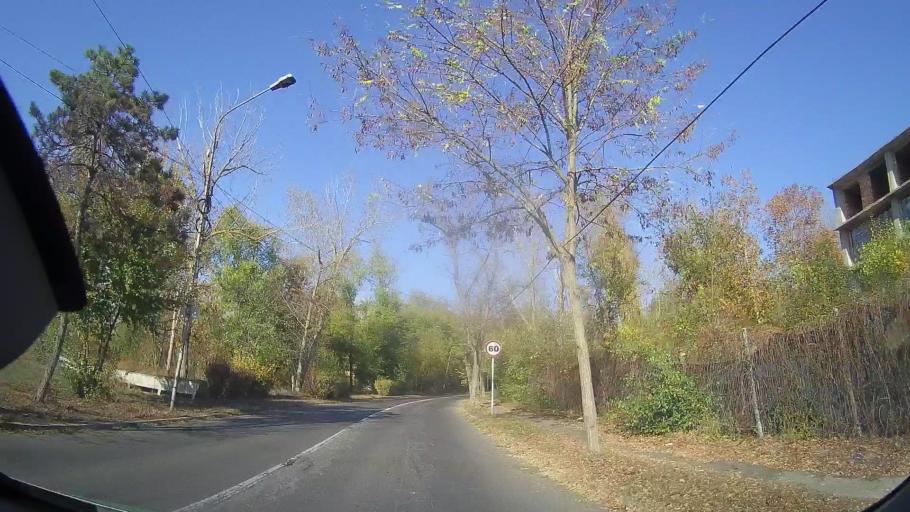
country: RO
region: Constanta
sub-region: Municipiul Mangalia
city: Mangalia
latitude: 43.8453
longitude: 28.5890
